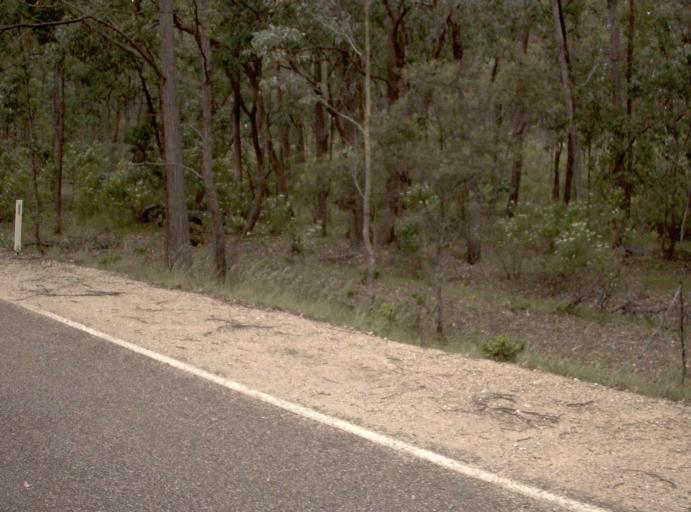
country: AU
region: Victoria
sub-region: East Gippsland
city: Bairnsdale
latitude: -37.7532
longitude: 147.3235
